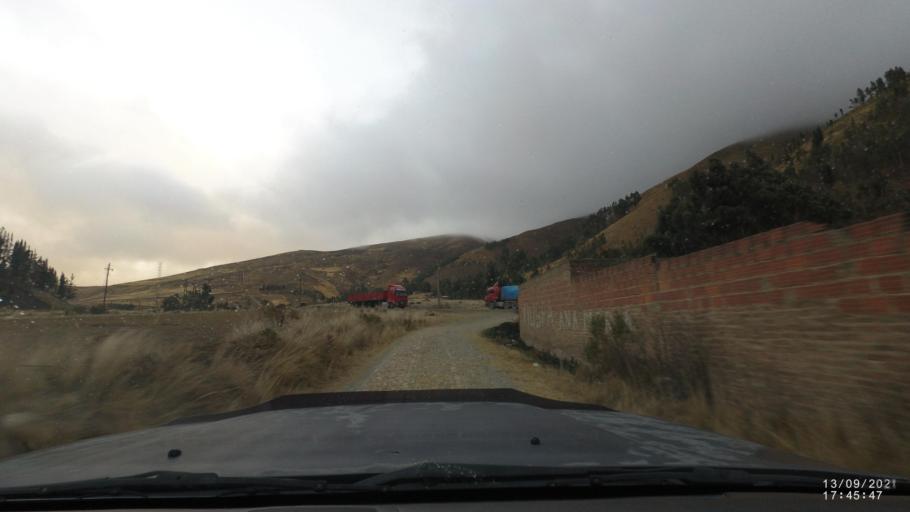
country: BO
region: Cochabamba
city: Colomi
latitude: -17.3796
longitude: -65.8339
